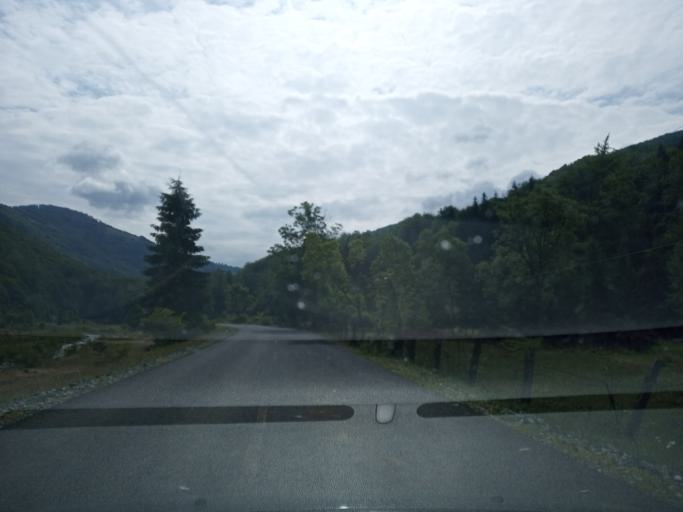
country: RO
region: Hunedoara
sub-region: Oras Petrila
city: Petrila
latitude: 45.4162
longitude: 23.4379
